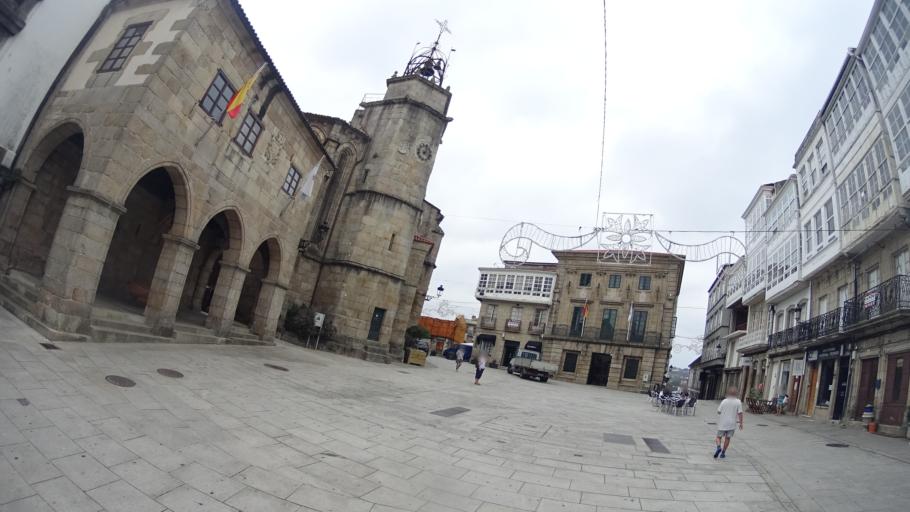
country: ES
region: Galicia
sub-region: Provincia da Coruna
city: Betanzos
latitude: 43.2810
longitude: -8.2111
